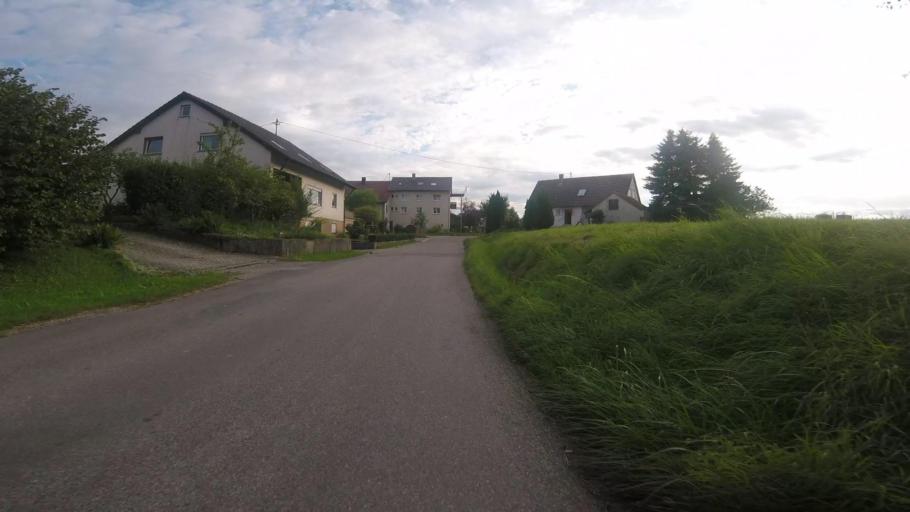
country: DE
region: Baden-Wuerttemberg
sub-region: Regierungsbezirk Stuttgart
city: Oberstenfeld
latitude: 49.0086
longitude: 9.3597
